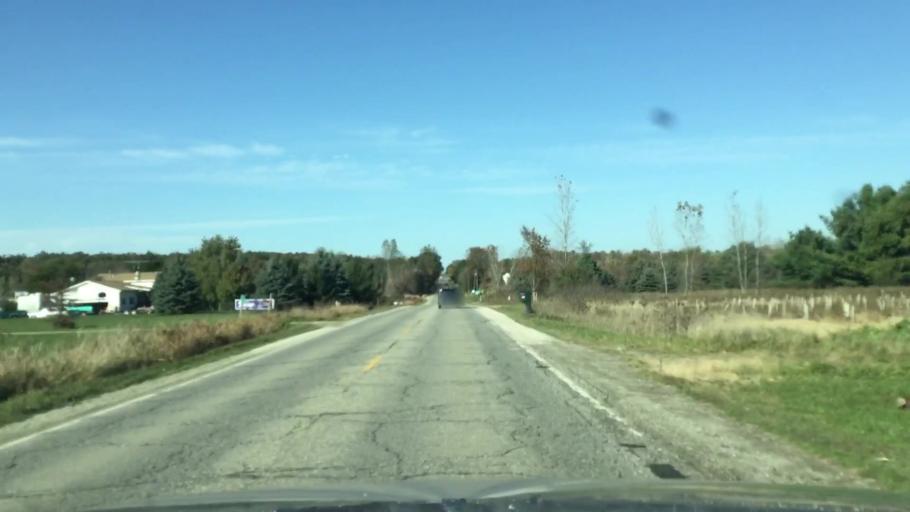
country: US
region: Michigan
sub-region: Lapeer County
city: Lapeer
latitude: 43.0686
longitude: -83.3436
